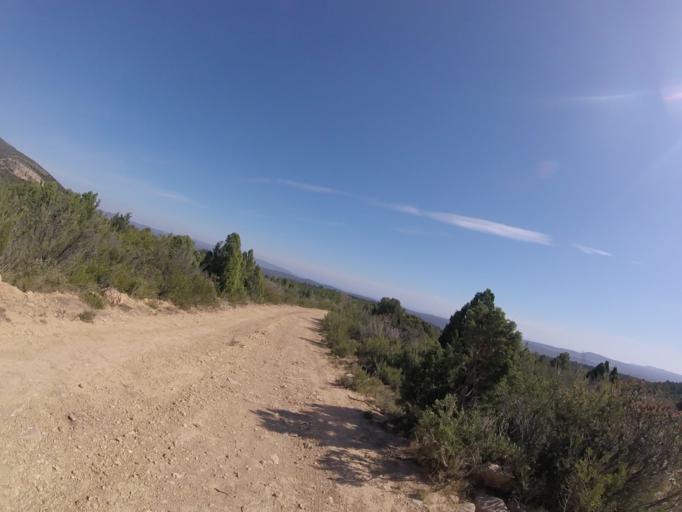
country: ES
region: Valencia
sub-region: Provincia de Castello
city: Sierra-Engarceran
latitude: 40.2717
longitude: 0.0219
